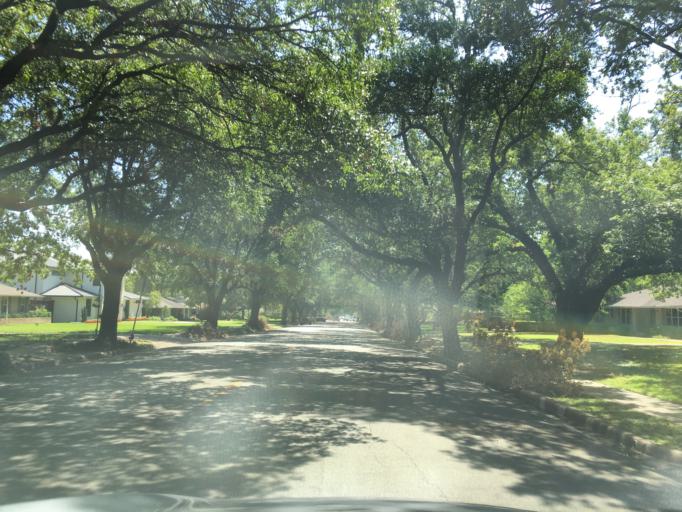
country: US
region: Texas
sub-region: Dallas County
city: University Park
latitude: 32.9002
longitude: -96.7824
